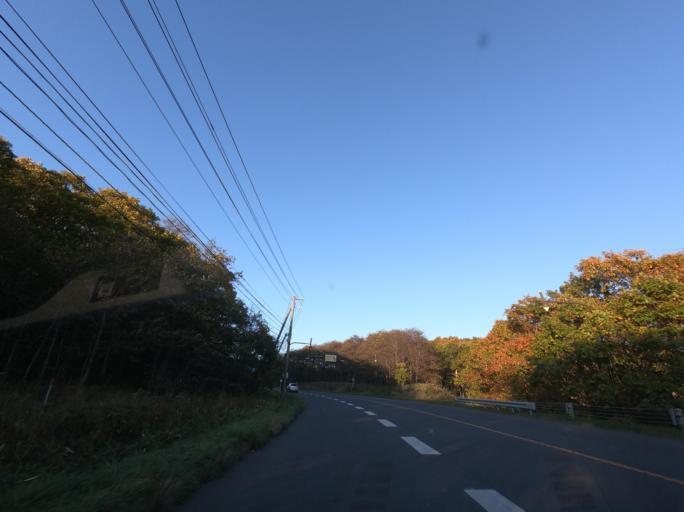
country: JP
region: Hokkaido
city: Kushiro
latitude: 43.0705
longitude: 144.3190
